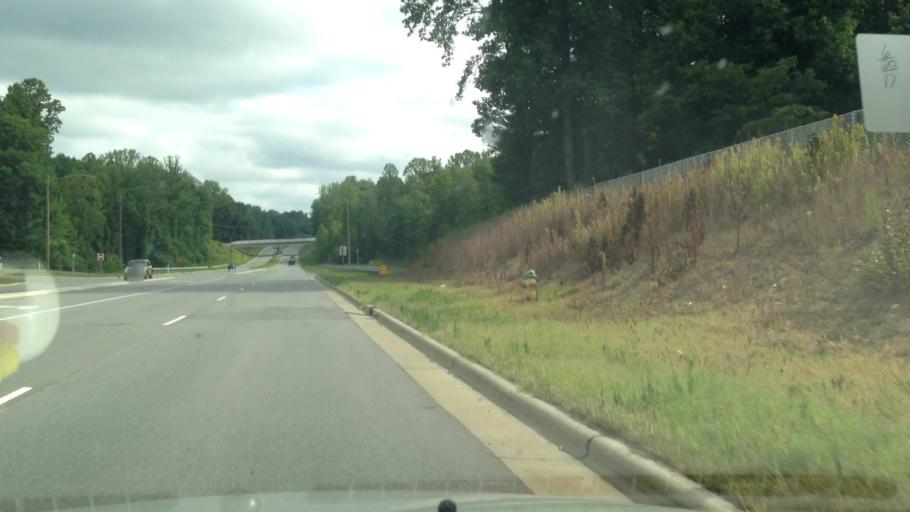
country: US
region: North Carolina
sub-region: Rockingham County
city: Reidsville
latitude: 36.3668
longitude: -79.6803
